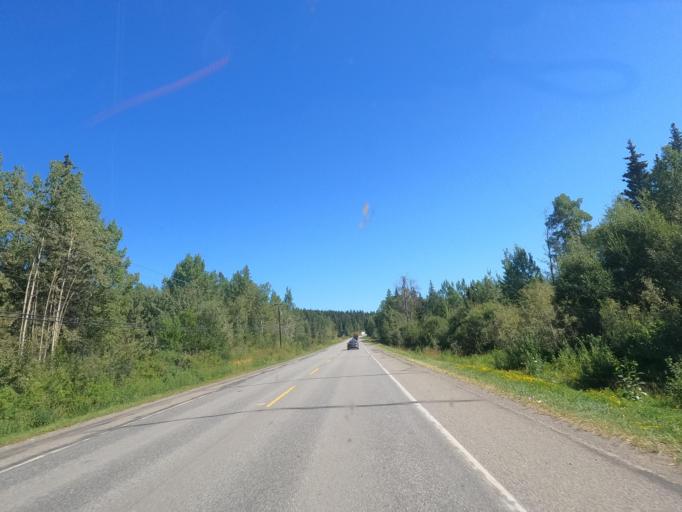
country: CA
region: British Columbia
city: Quesnel
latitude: 53.0435
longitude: -122.4708
